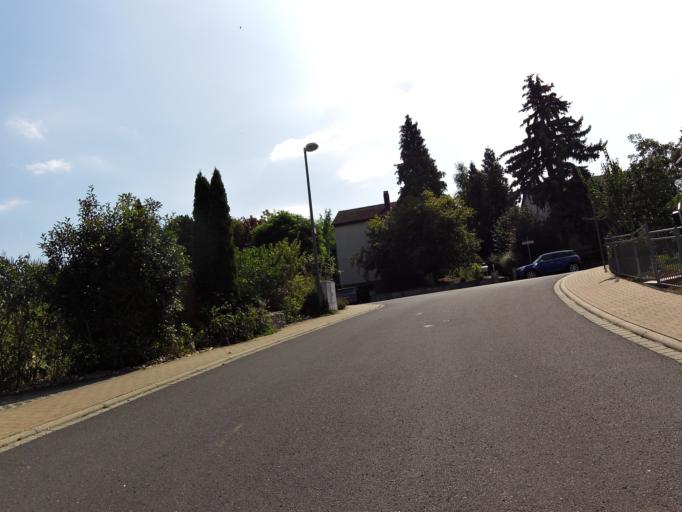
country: DE
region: Bavaria
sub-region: Regierungsbezirk Unterfranken
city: Zell am Main
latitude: 49.8122
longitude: 9.8654
